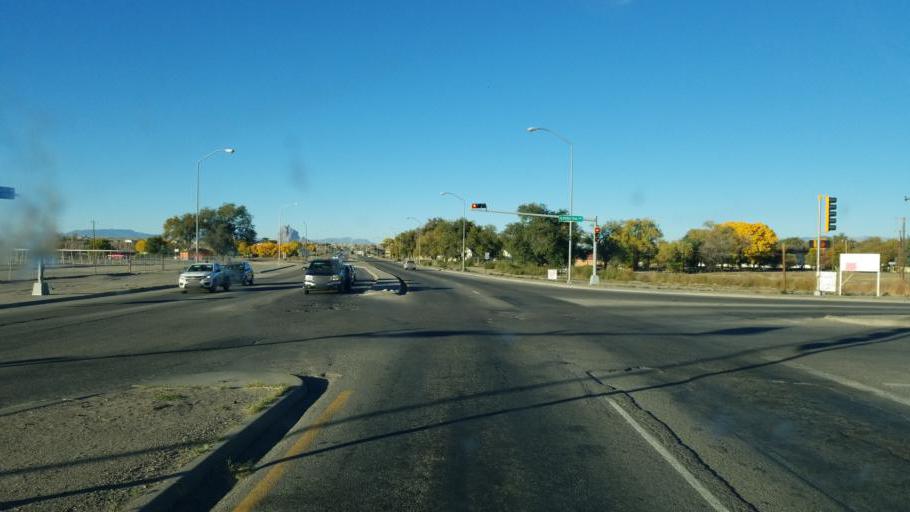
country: US
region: New Mexico
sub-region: San Juan County
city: Shiprock
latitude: 36.7850
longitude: -108.6848
